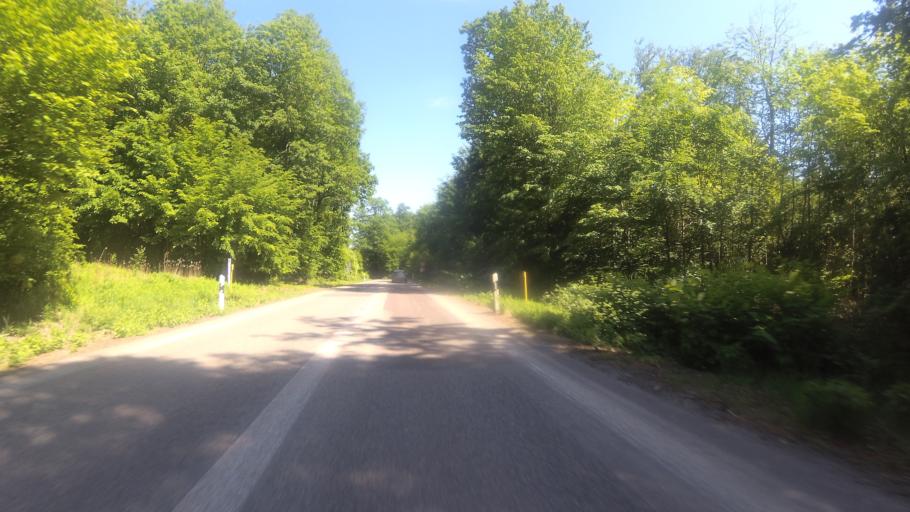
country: DE
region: Saarland
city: Quierschied
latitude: 49.3086
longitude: 7.0199
